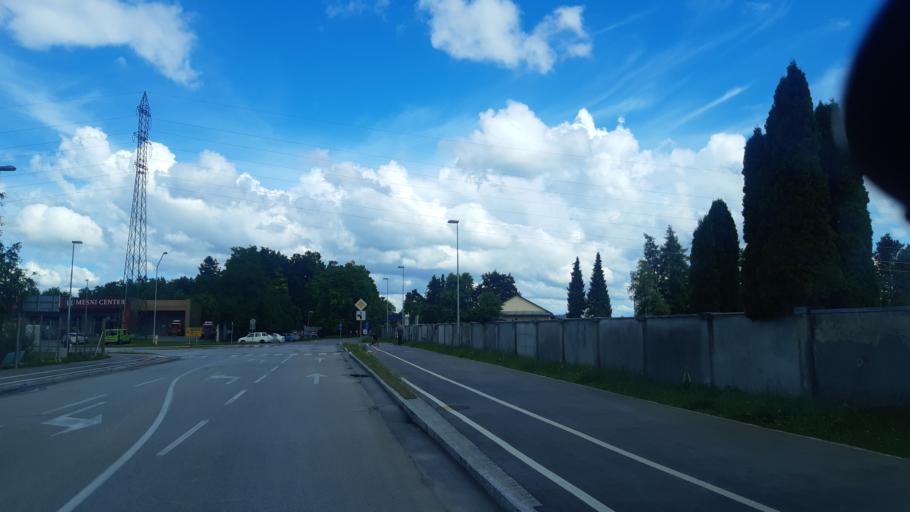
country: SI
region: Kranj
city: Kranj
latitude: 46.2365
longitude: 14.3677
